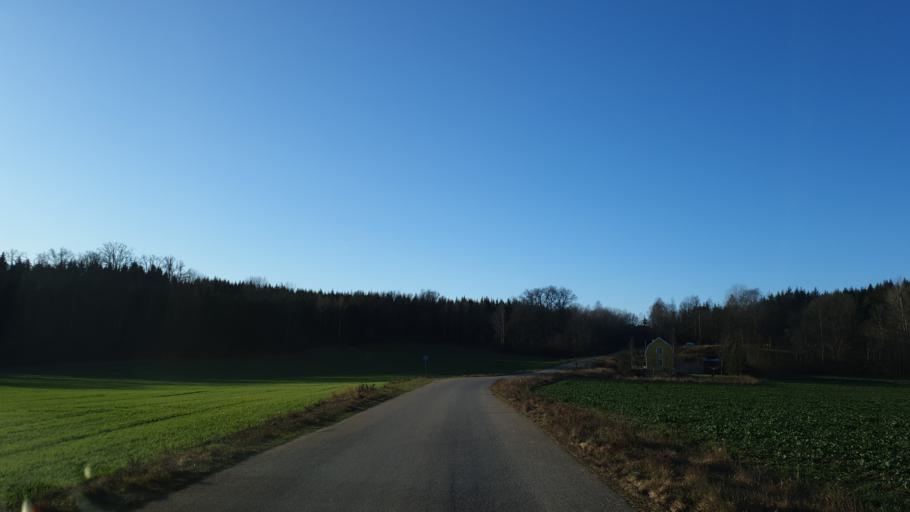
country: SE
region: Blekinge
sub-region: Karlskrona Kommun
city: Nattraby
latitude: 56.2631
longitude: 15.4981
